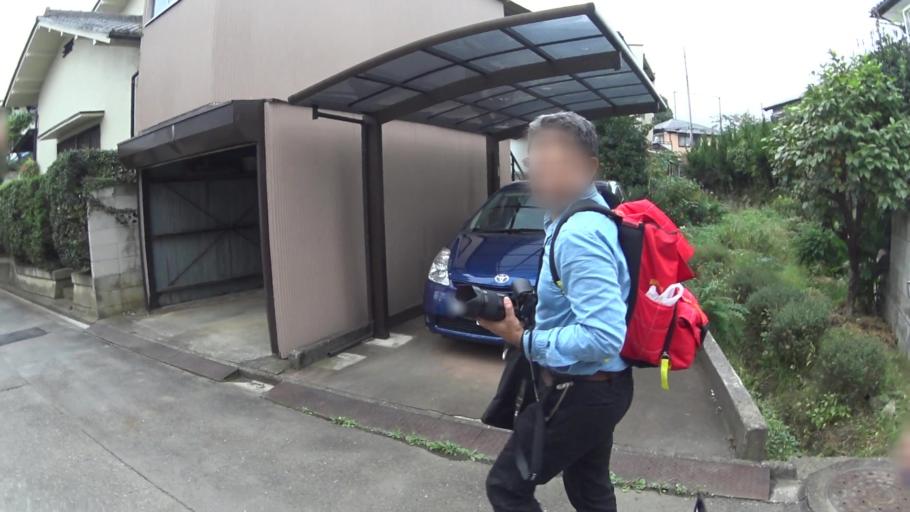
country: JP
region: Saitama
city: Hanno
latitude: 35.8592
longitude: 139.3198
